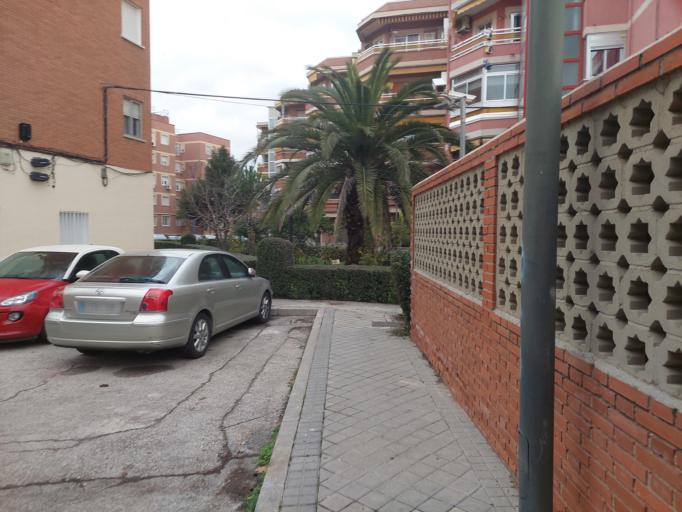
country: ES
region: Madrid
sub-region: Provincia de Madrid
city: Leganes
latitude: 40.3272
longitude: -3.7692
